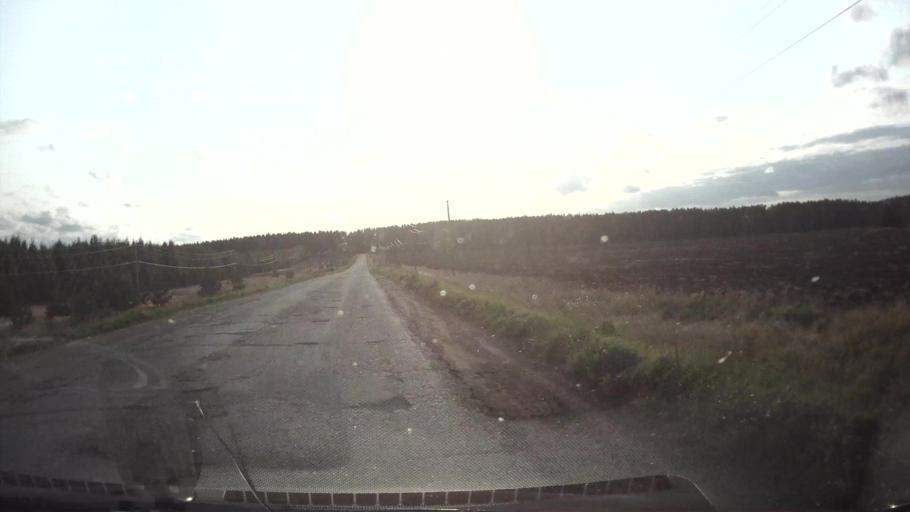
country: RU
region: Mariy-El
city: Kuzhener
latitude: 56.9529
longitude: 48.7574
